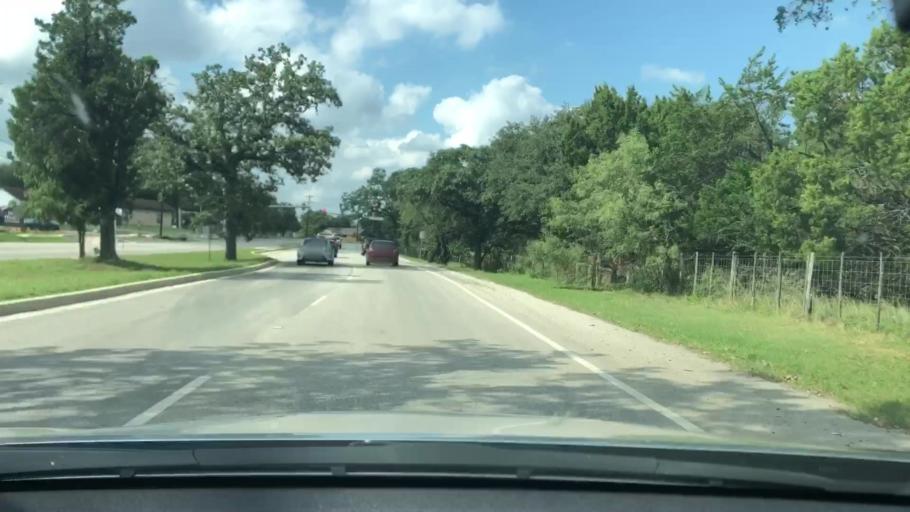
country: US
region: Texas
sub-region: Kendall County
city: Boerne
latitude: 29.7821
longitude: -98.7165
